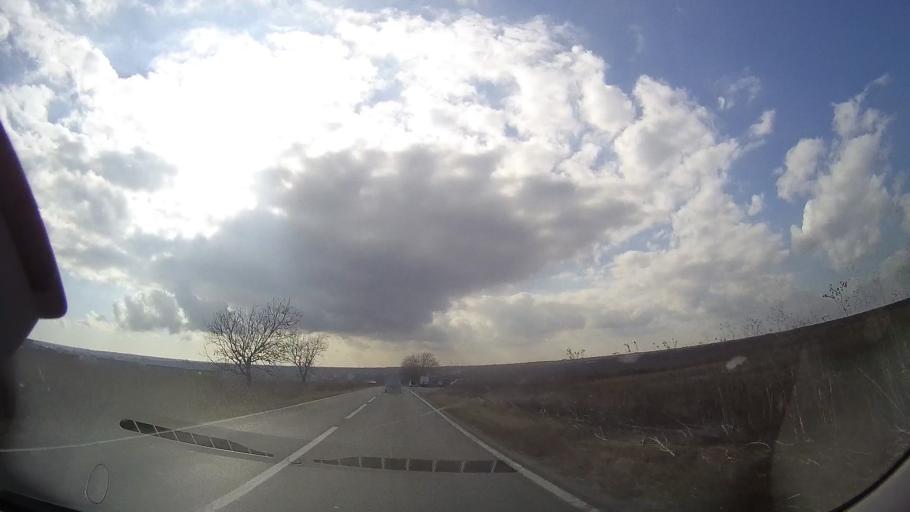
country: RO
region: Constanta
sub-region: Oras Techirghiol
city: Techirghiol
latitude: 44.0705
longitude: 28.5962
